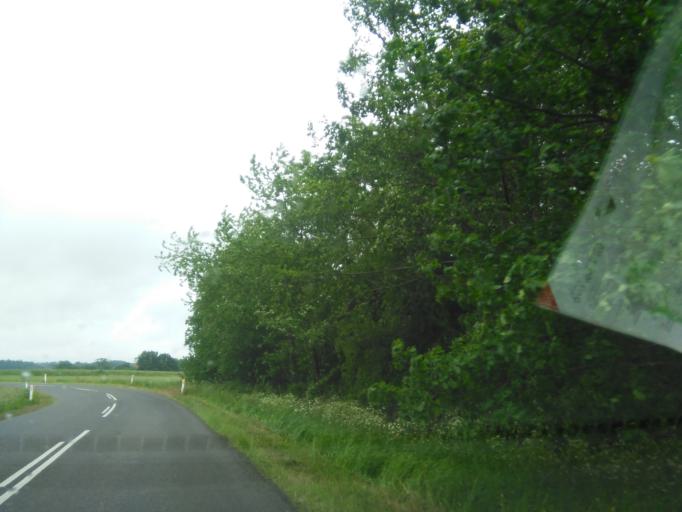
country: DK
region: Capital Region
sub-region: Bornholm Kommune
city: Ronne
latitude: 55.2403
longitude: 14.7453
